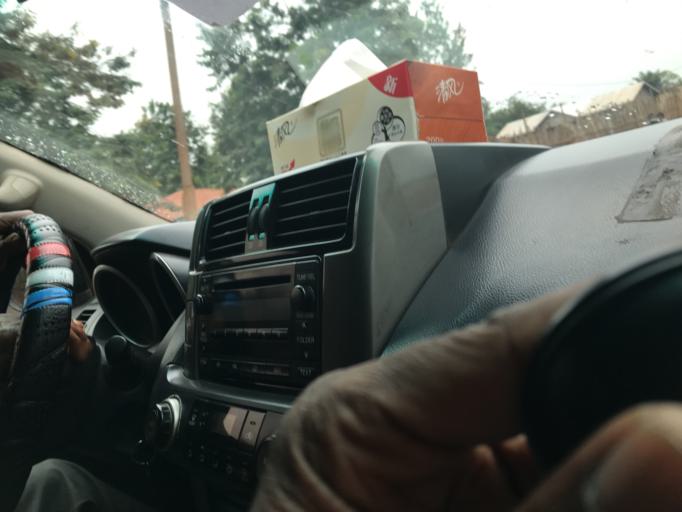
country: CD
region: Equateur
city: Gemena
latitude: 3.2384
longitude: 19.7803
